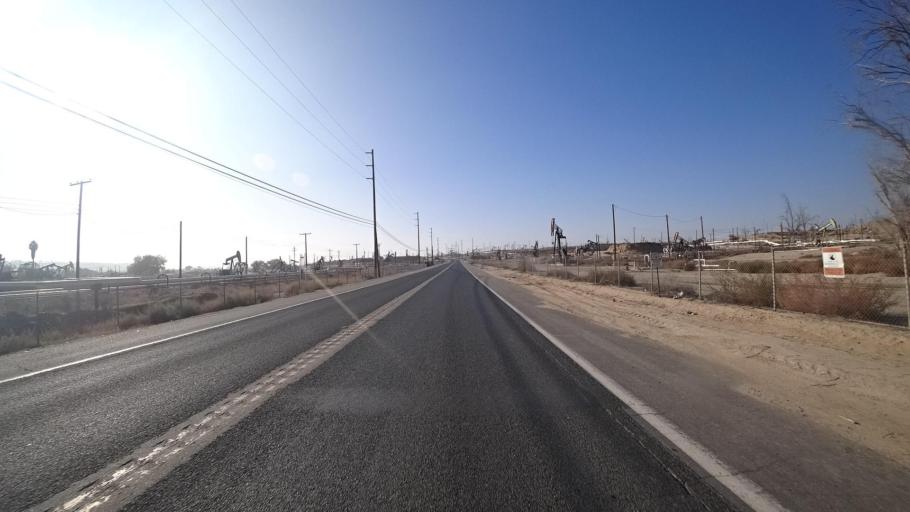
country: US
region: California
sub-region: Kern County
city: Oildale
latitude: 35.4279
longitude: -118.9708
